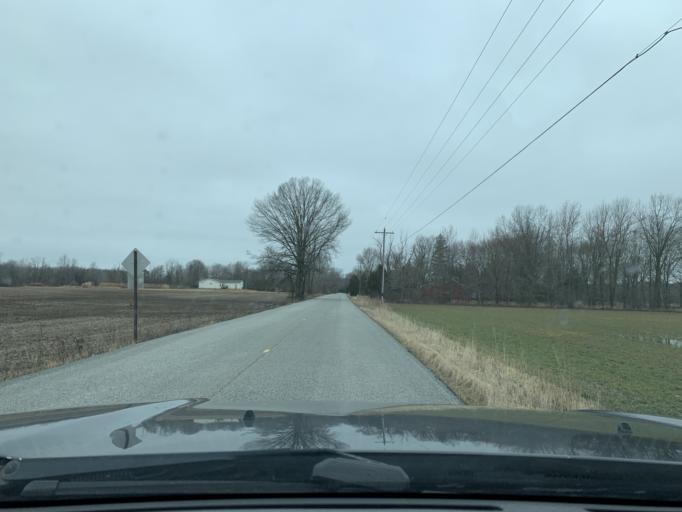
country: US
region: Indiana
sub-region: Porter County
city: Chesterton
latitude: 41.6106
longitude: -87.0055
